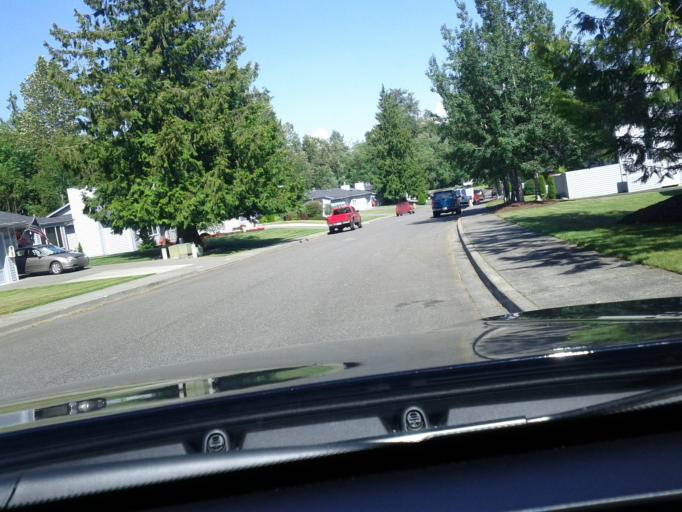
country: US
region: Washington
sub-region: Skagit County
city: Burlington
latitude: 48.4459
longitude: -122.3056
